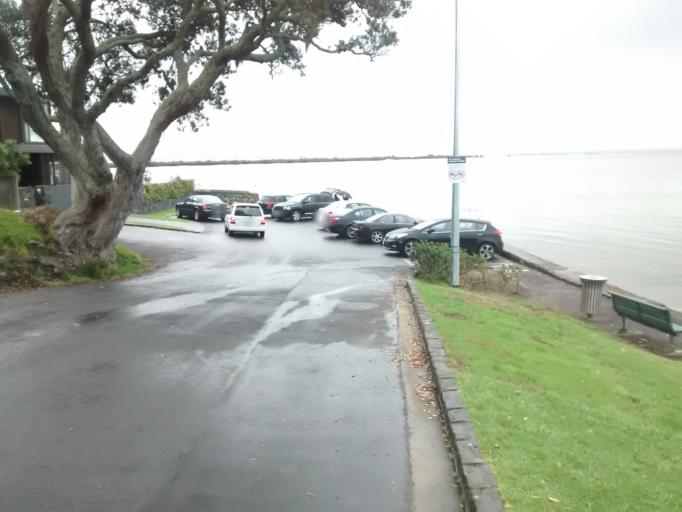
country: NZ
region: Auckland
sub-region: Auckland
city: Rosebank
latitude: -36.8520
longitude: 174.7154
